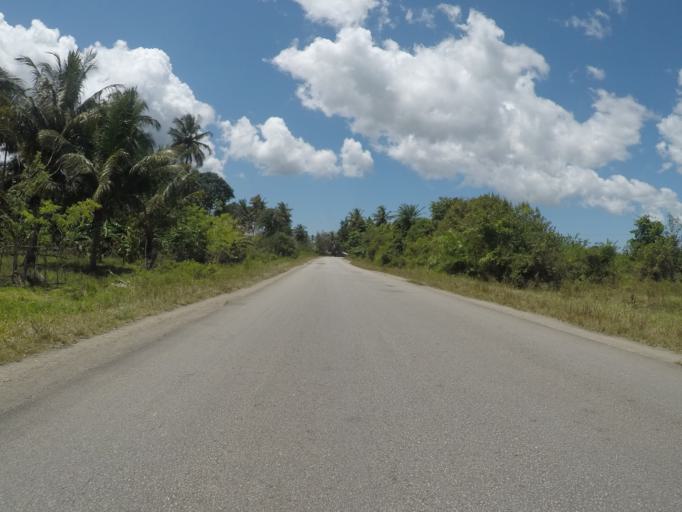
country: TZ
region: Zanzibar Central/South
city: Nganane
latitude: -6.2704
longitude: 39.4244
